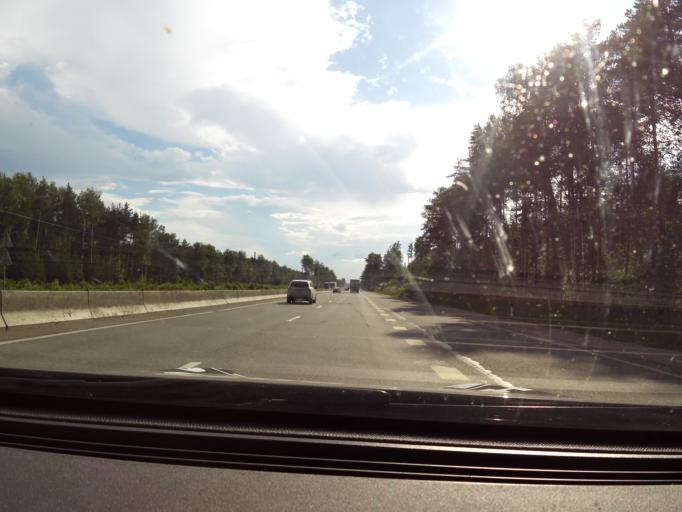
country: RU
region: Nizjnij Novgorod
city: Mulino
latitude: 56.2561
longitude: 42.8979
